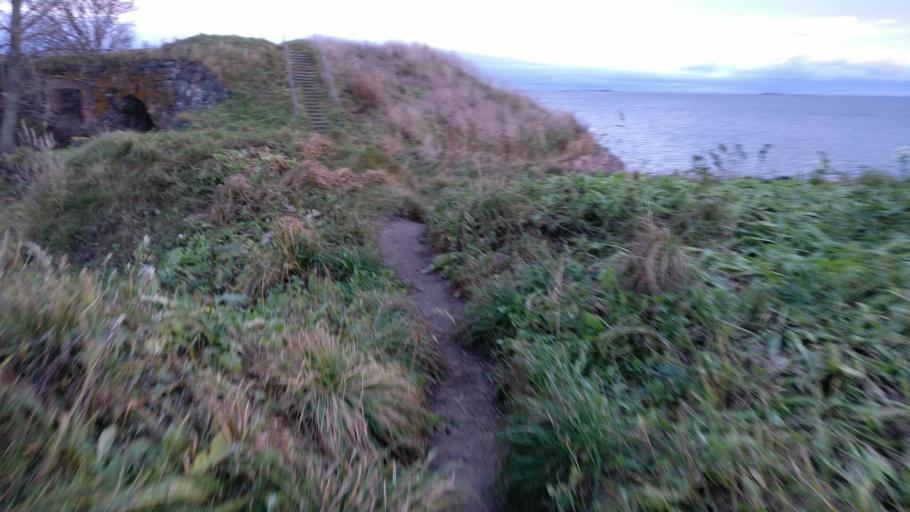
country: FI
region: Uusimaa
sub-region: Helsinki
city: Helsinki
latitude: 60.1424
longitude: 24.9809
